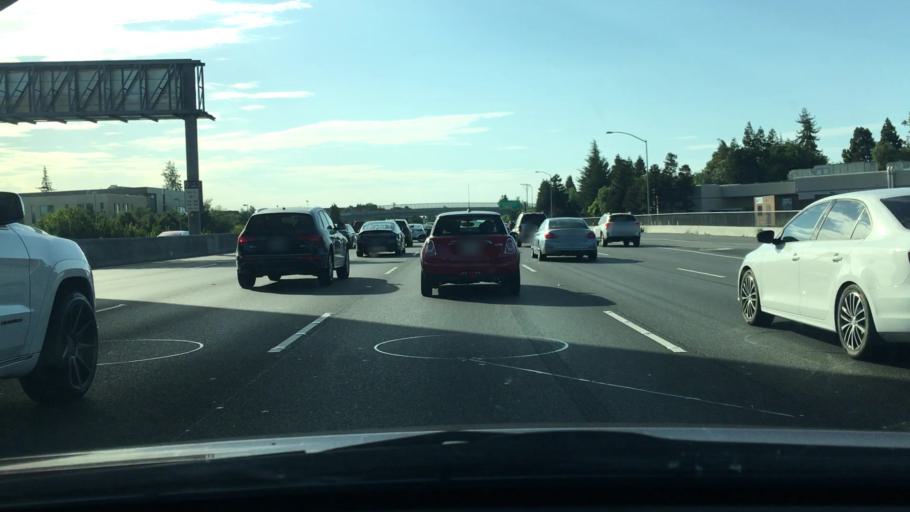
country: US
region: California
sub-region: Santa Clara County
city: Mountain View
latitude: 37.4150
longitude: -122.0831
